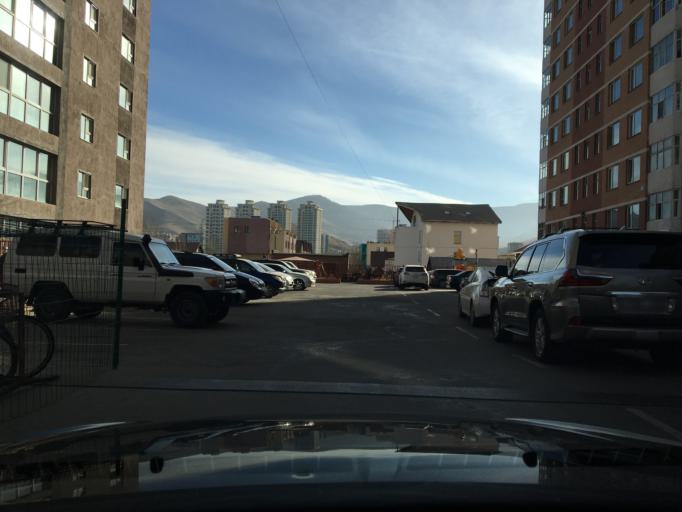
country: MN
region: Ulaanbaatar
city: Ulaanbaatar
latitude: 47.8946
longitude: 106.9129
